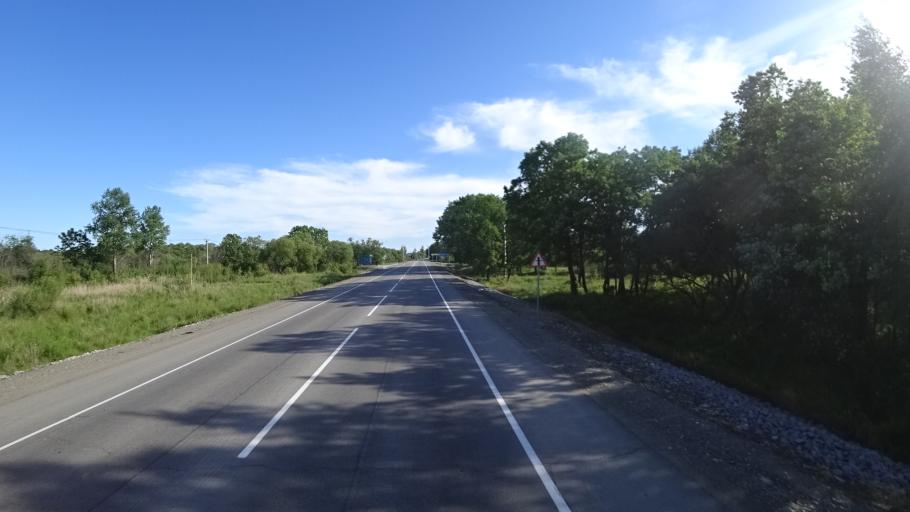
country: RU
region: Khabarovsk Krai
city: Khor
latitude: 47.8582
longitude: 134.9625
